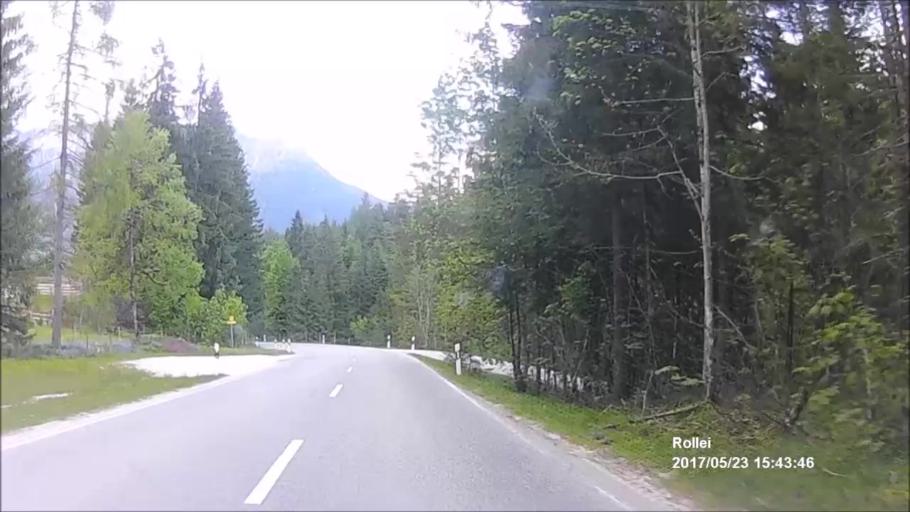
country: DE
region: Bavaria
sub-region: Upper Bavaria
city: Bischofswiesen
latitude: 47.6451
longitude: 12.9220
